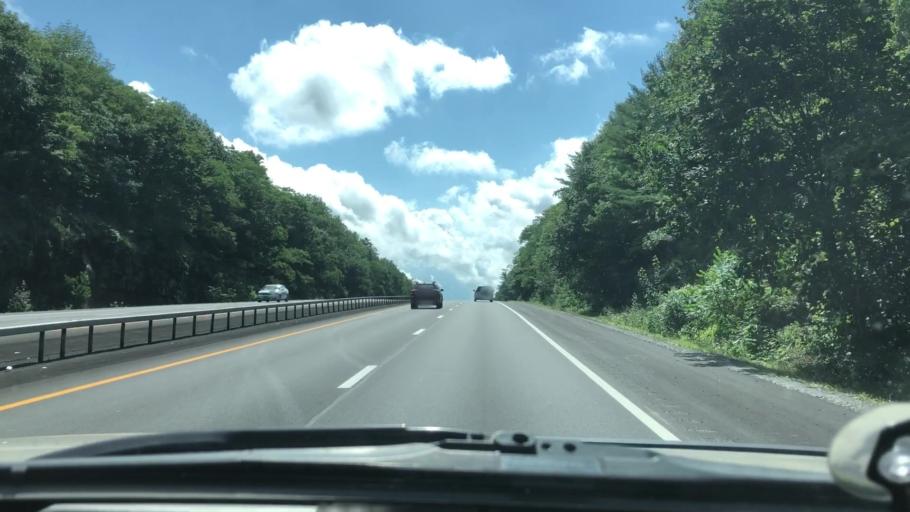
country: US
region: New York
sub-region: Greene County
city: Cairo
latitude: 42.3057
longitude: -74.0005
